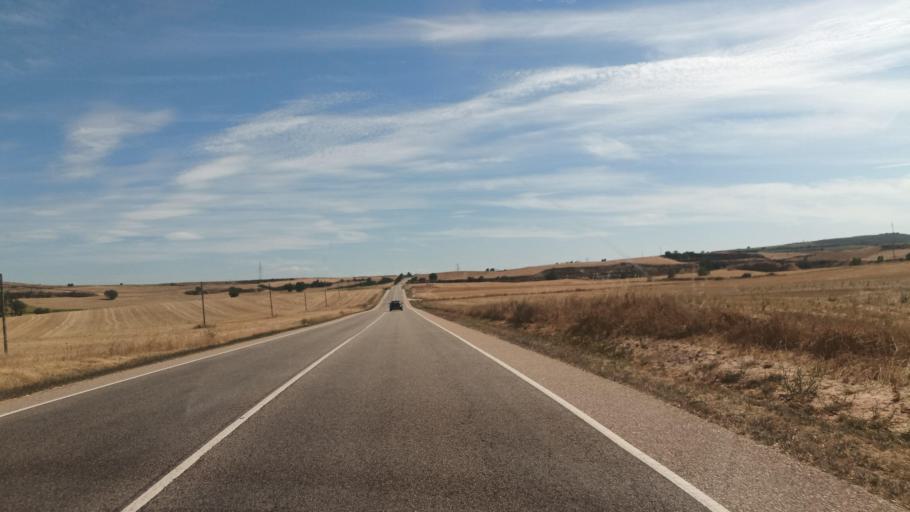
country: ES
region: Castille and Leon
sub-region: Provincia de Burgos
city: Aguilar de Bureba
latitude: 42.5817
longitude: -3.3363
